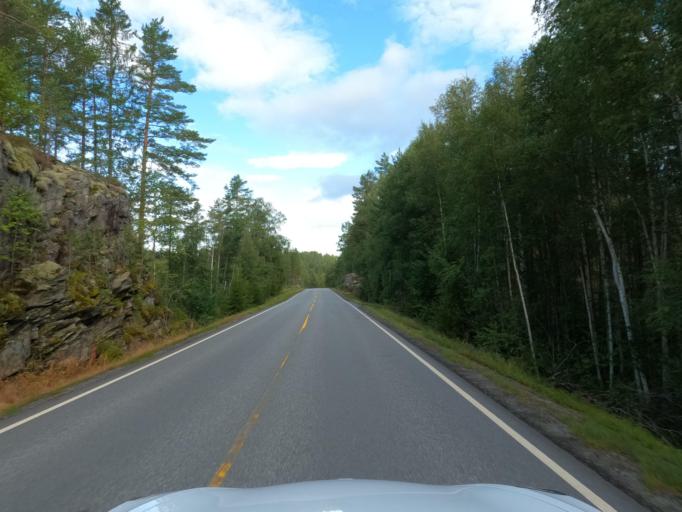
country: NO
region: Telemark
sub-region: Notodden
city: Notodden
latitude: 59.7376
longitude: 9.1544
